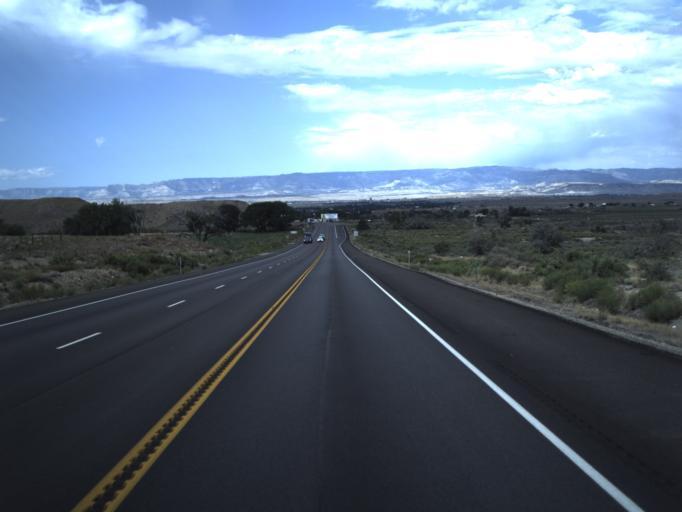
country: US
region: Utah
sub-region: Carbon County
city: Wellington
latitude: 39.5505
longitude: -110.6614
